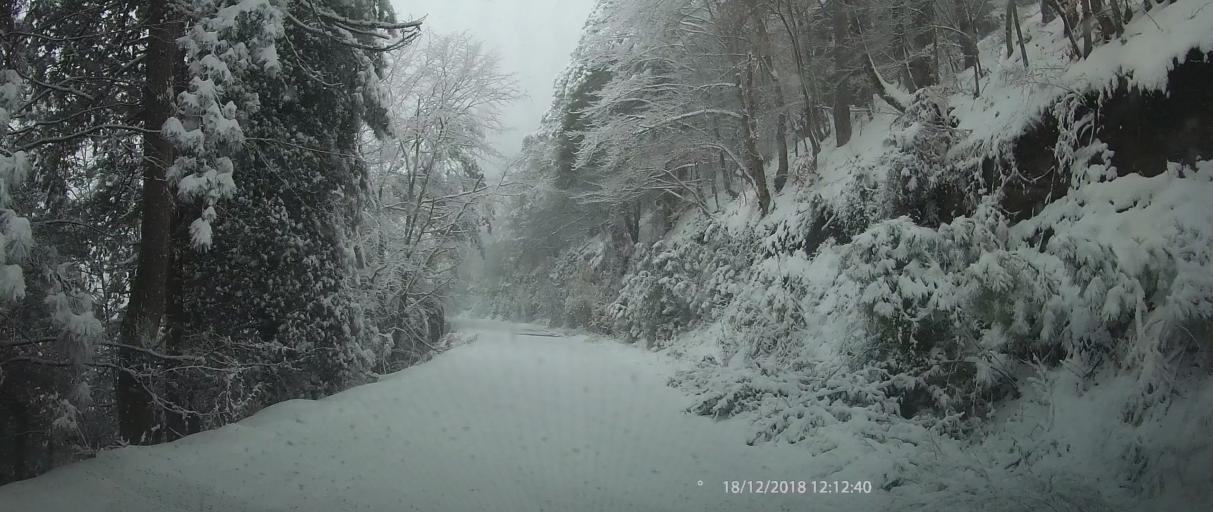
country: GR
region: Central Macedonia
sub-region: Nomos Pierias
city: Litochoro
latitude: 40.1031
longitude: 22.4413
